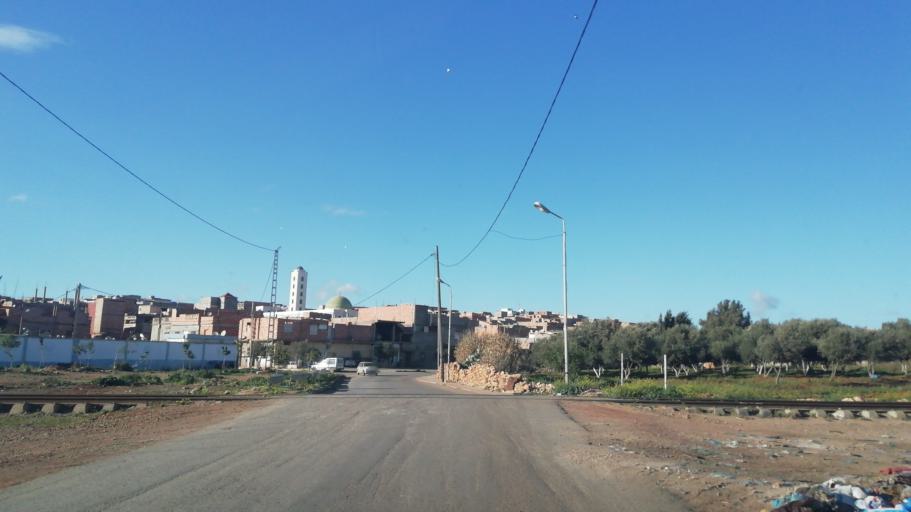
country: DZ
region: Oran
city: Sidi ech Chahmi
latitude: 35.6881
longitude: -0.4960
